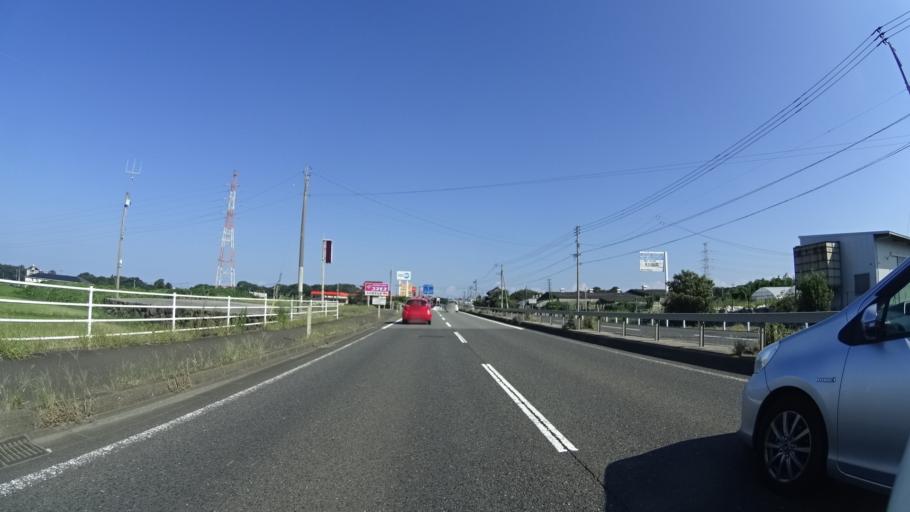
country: JP
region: Fukuoka
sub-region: Buzen-shi
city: Buzen
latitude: 33.6108
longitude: 131.1075
